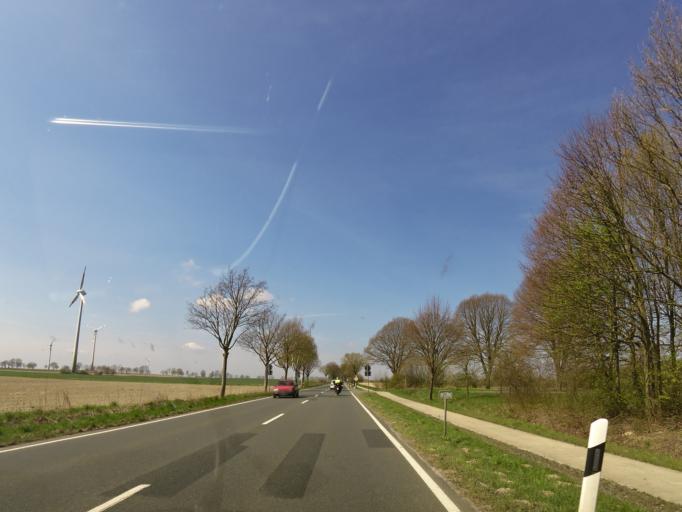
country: DE
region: Lower Saxony
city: Wunstorf
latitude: 52.4323
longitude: 9.3893
